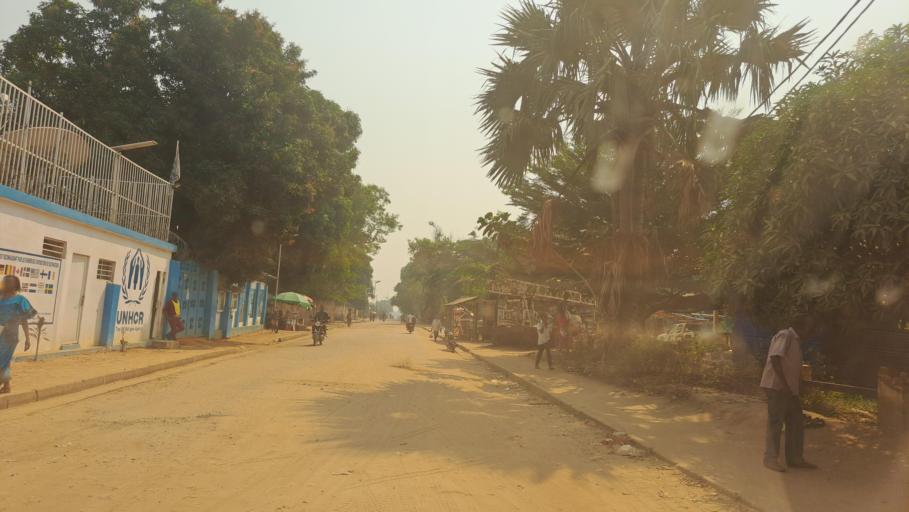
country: CD
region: Kasai-Occidental
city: Kananga
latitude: -5.9016
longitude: 22.4061
